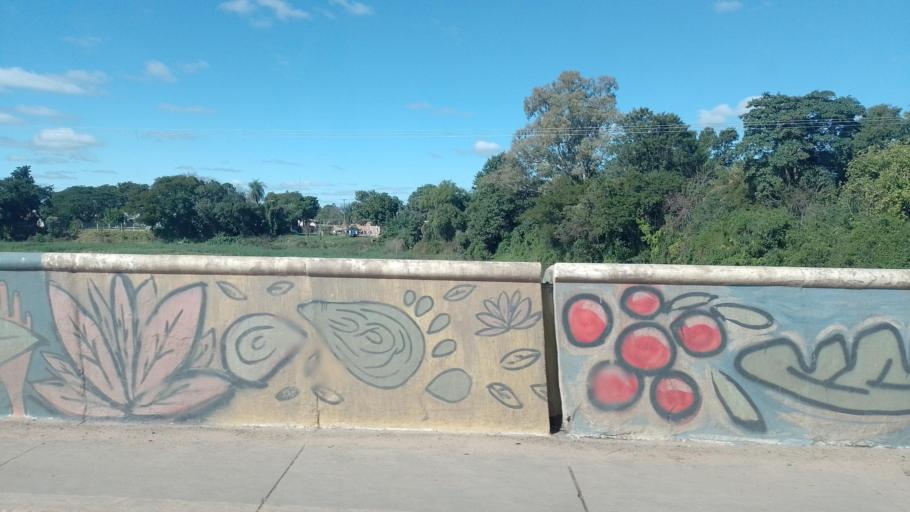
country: AR
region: Chaco
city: Resistencia
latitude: -27.4369
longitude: -58.9794
